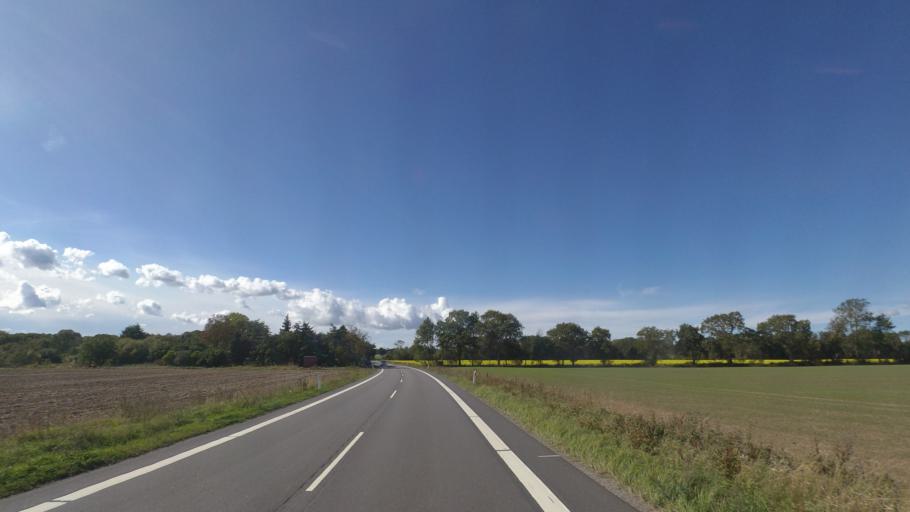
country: DK
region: Capital Region
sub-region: Bornholm Kommune
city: Akirkeby
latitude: 55.0693
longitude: 14.9828
